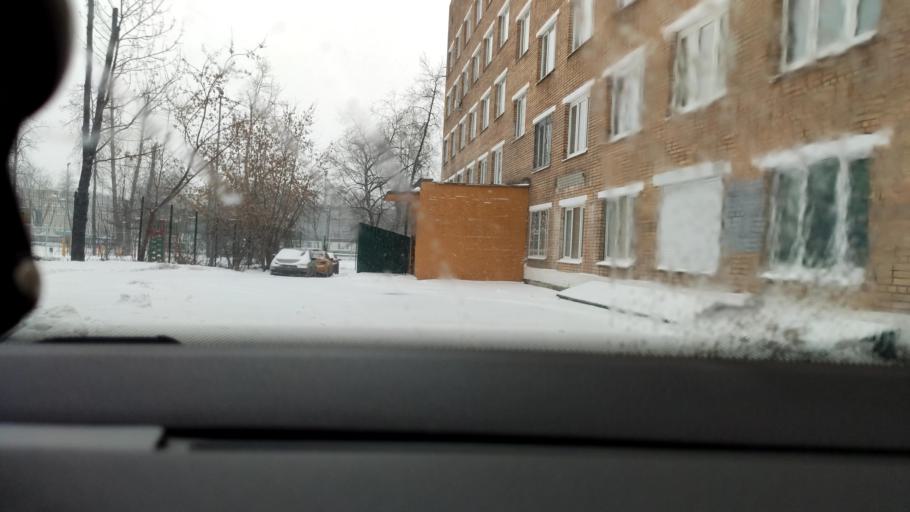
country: RU
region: Moscow
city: Ryazanskiy
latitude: 55.7395
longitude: 37.7401
